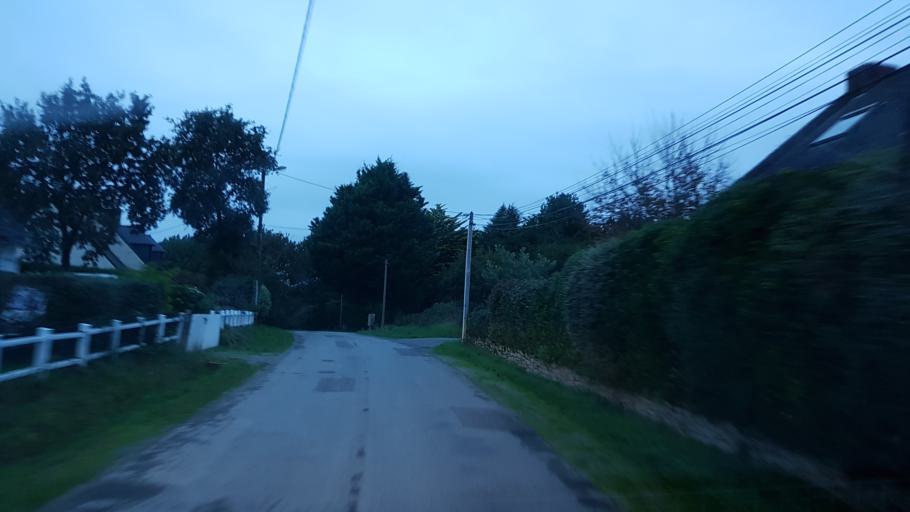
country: FR
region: Brittany
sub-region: Departement du Morbihan
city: Sarzeau
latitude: 47.5426
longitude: -2.8126
